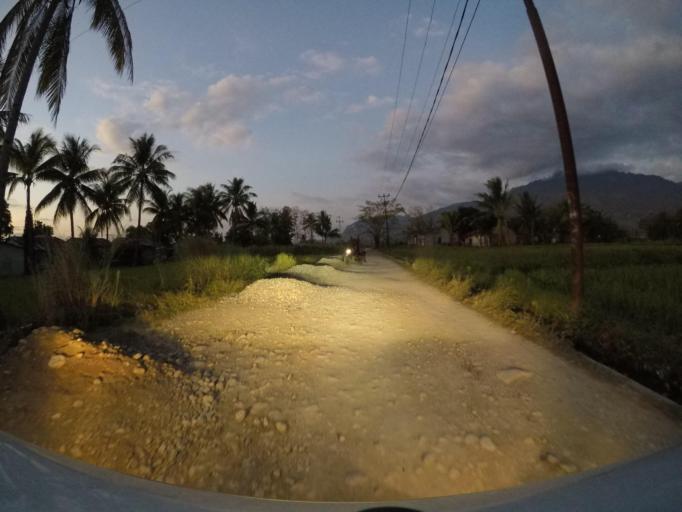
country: TL
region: Bobonaro
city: Maliana
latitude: -8.9845
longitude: 125.2109
